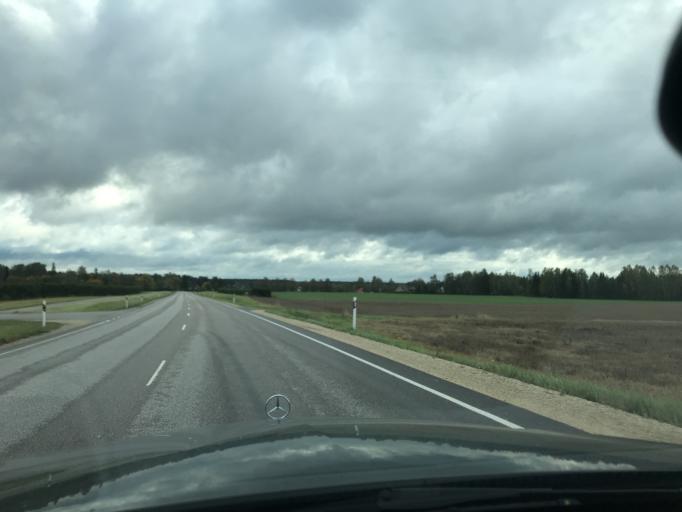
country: EE
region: Valgamaa
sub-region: Torva linn
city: Torva
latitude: 58.0089
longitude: 25.9013
